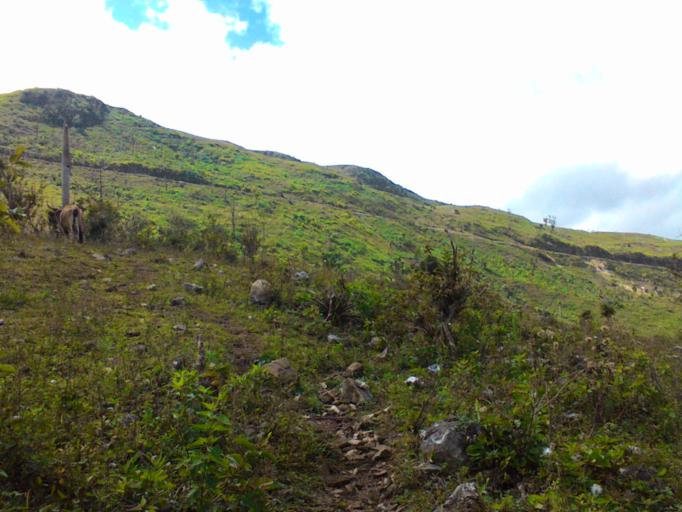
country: HT
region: Grandans
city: Moron
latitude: 18.4521
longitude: -74.1053
